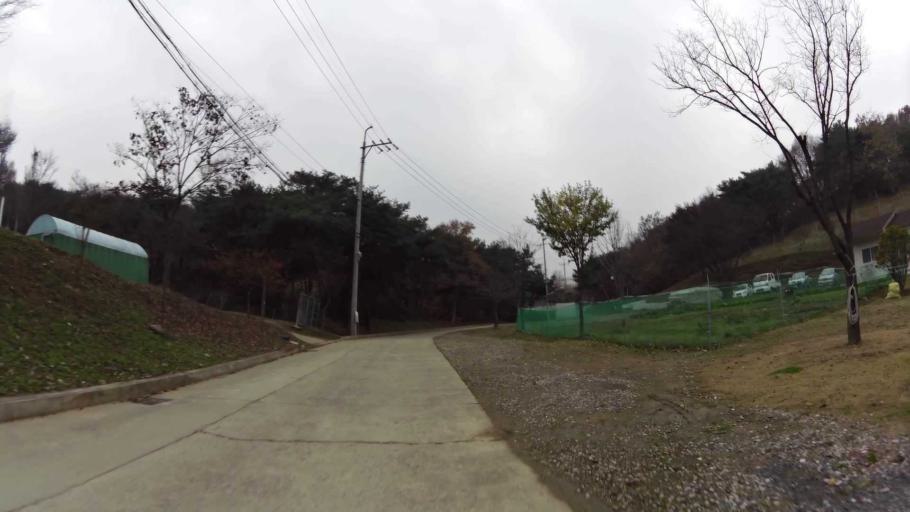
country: KR
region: Daegu
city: Daegu
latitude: 35.8590
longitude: 128.6612
